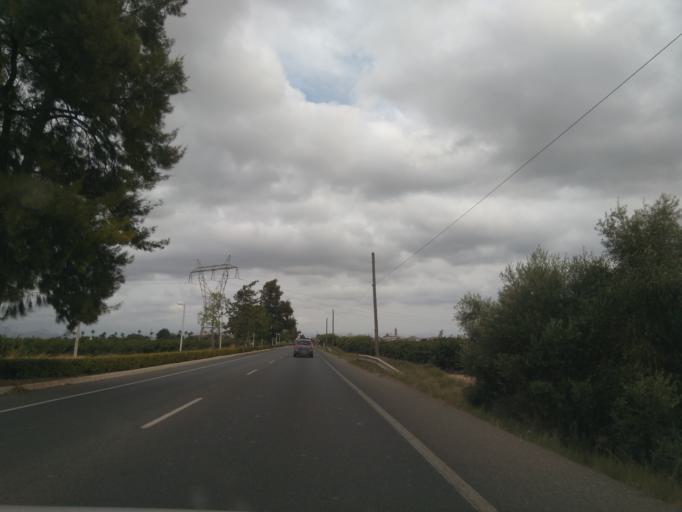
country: ES
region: Valencia
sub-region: Provincia de Valencia
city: L'Alcudia
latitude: 39.2125
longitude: -0.5130
